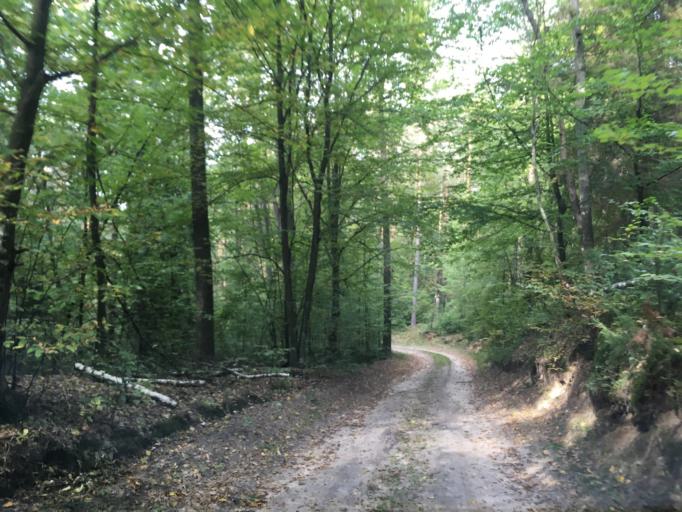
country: PL
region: Kujawsko-Pomorskie
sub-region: Powiat brodnicki
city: Gorzno
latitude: 53.2216
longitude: 19.7063
